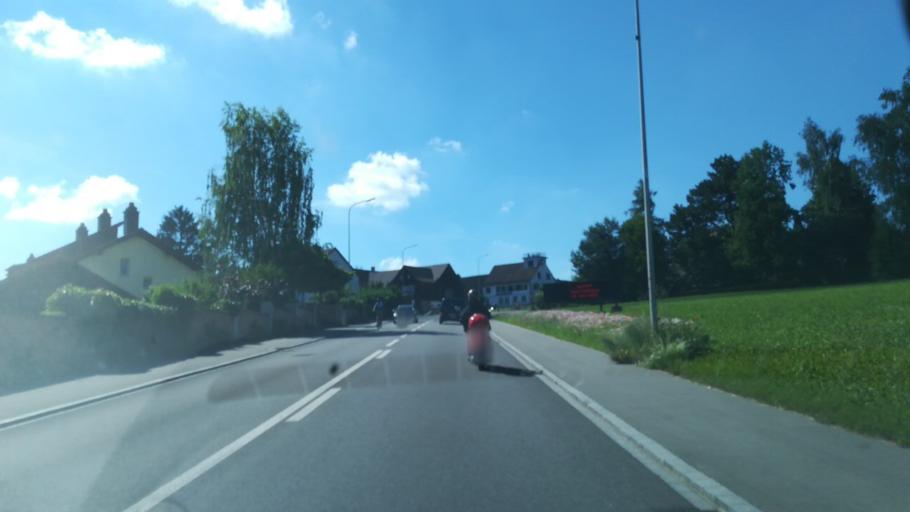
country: CH
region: Thurgau
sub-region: Weinfelden District
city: Berg
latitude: 47.5759
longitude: 9.1673
